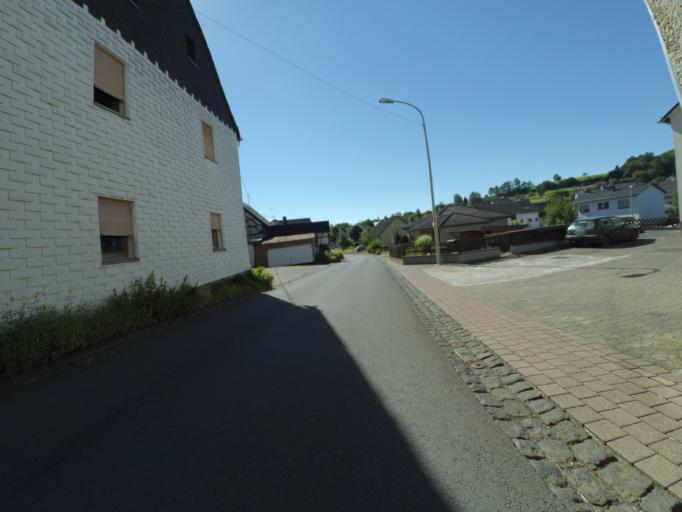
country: DE
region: Rheinland-Pfalz
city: Schonbach
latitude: 50.2161
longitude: 6.9482
